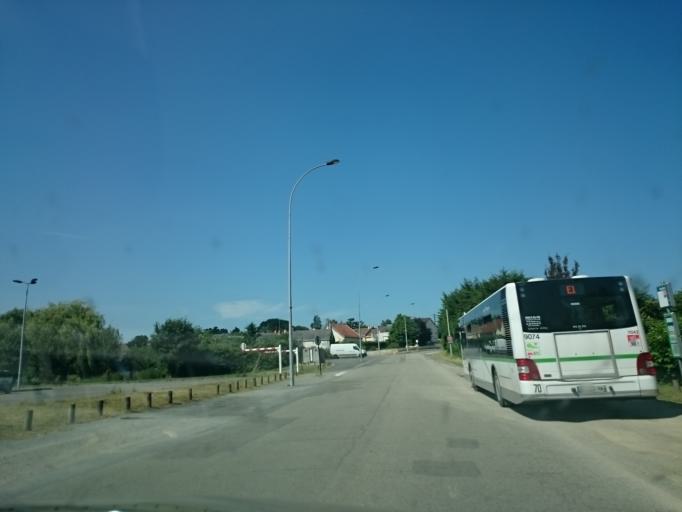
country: FR
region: Pays de la Loire
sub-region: Departement de la Loire-Atlantique
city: Coueron
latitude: 47.2119
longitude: -1.7357
